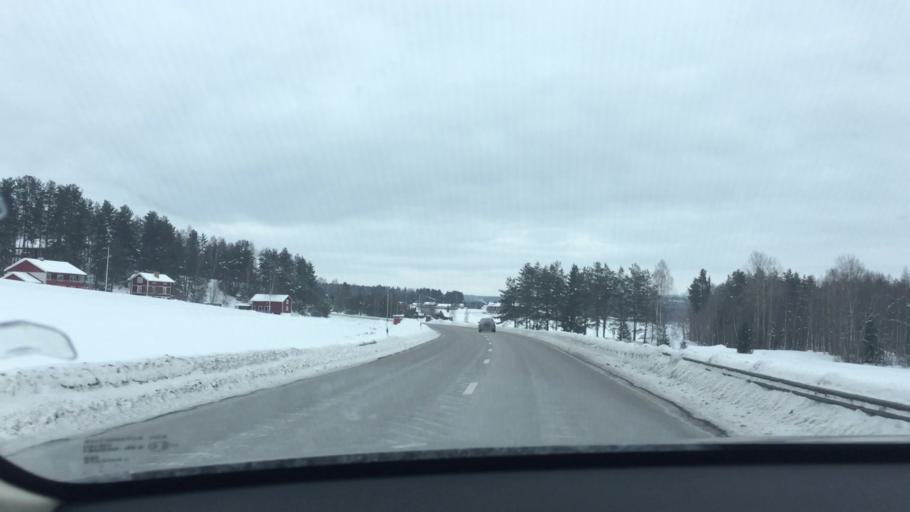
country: SE
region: Dalarna
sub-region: Faluns Kommun
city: Svardsjo
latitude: 60.6285
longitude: 15.8282
